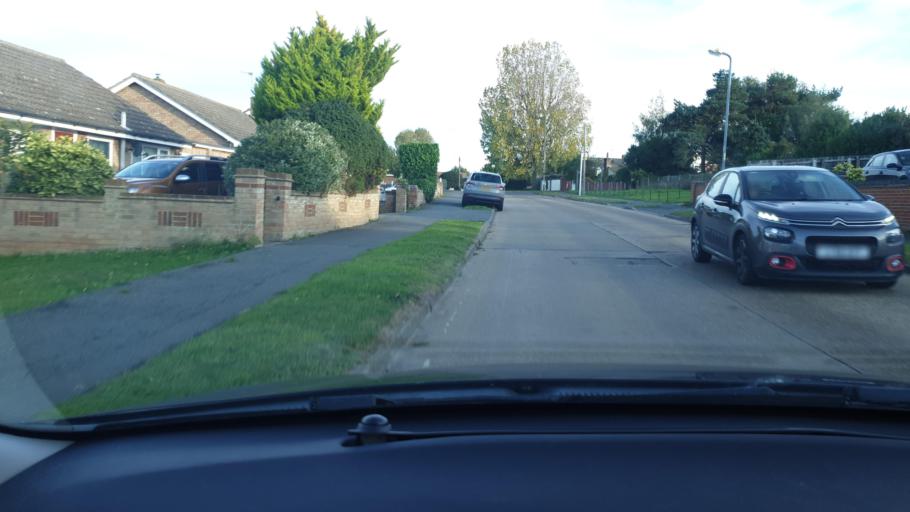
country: GB
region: England
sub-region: Essex
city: Brightlingsea
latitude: 51.7940
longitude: 1.0345
